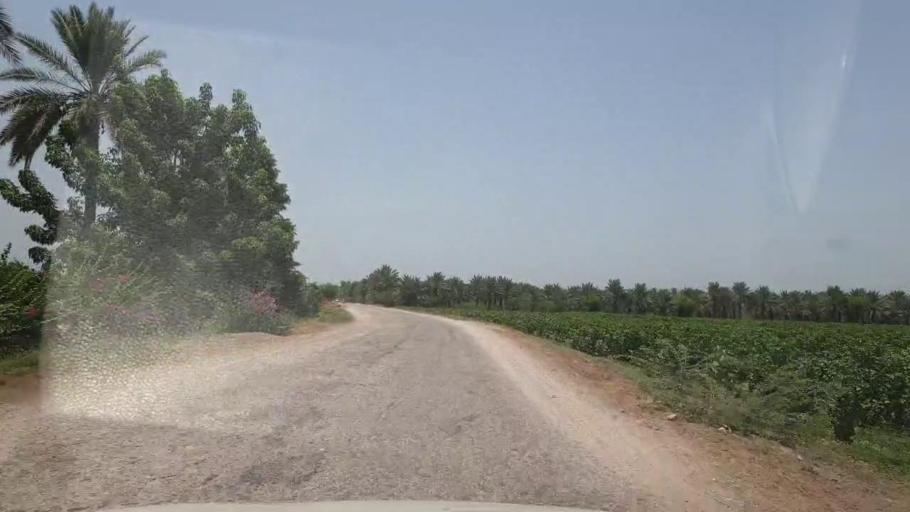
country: PK
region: Sindh
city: Bozdar
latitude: 27.1885
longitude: 68.6032
